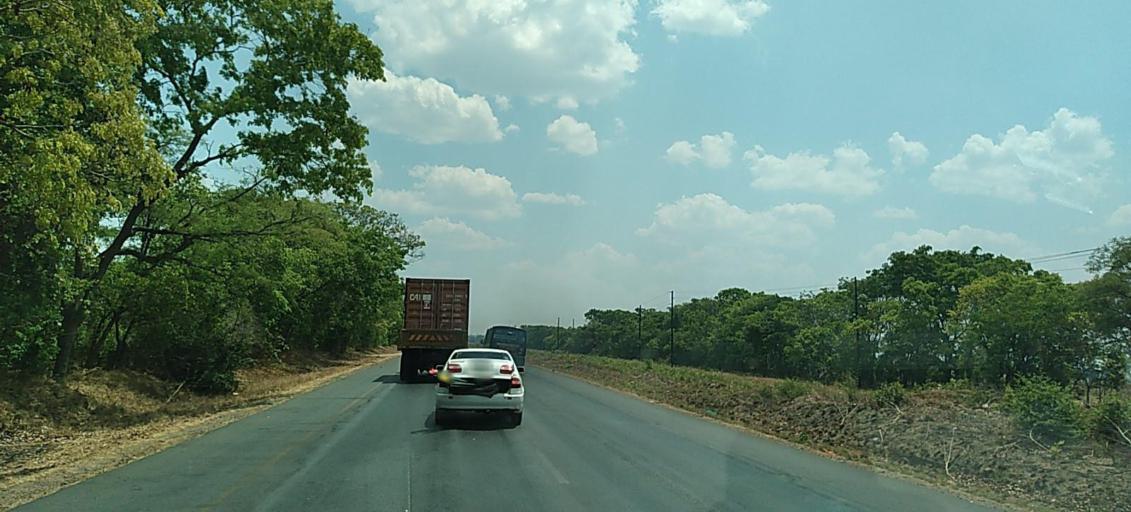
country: ZM
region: Central
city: Kabwe
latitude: -14.3377
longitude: 28.5308
